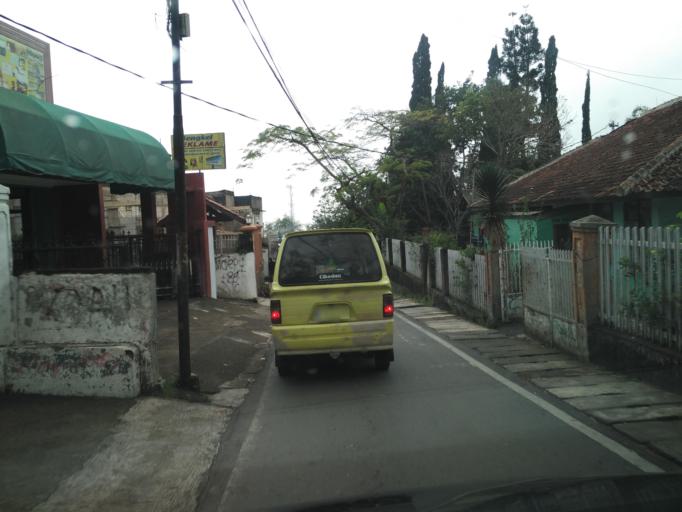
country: ID
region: West Java
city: Caringin
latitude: -6.7280
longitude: 107.0367
